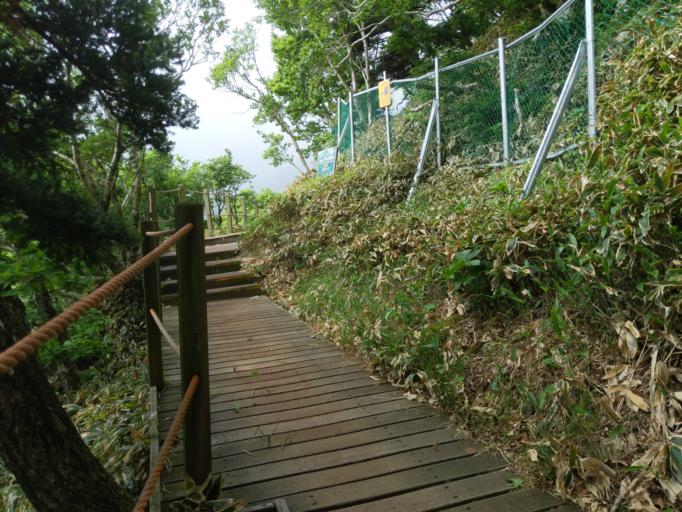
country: KR
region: Jeju-do
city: Seogwipo
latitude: 33.3755
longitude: 126.5303
